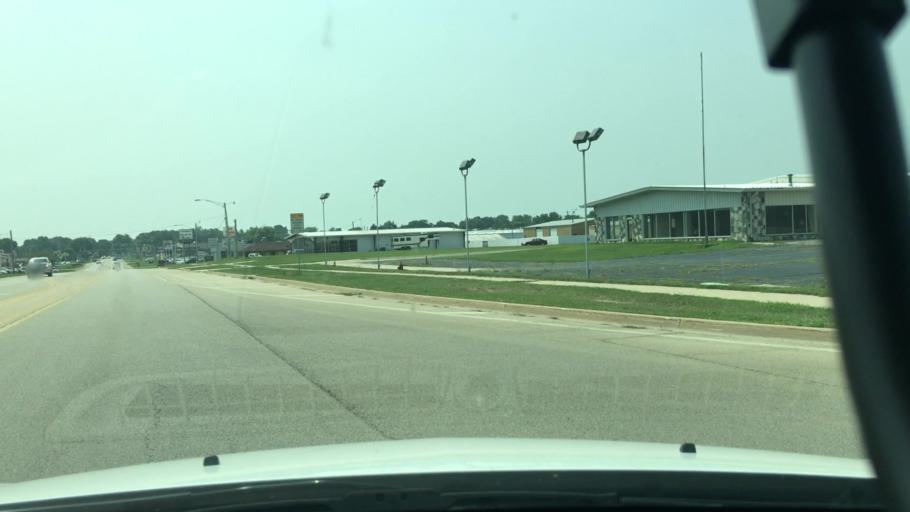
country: US
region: Illinois
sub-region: Ogle County
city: Hillcrest
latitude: 41.9409
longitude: -89.0681
